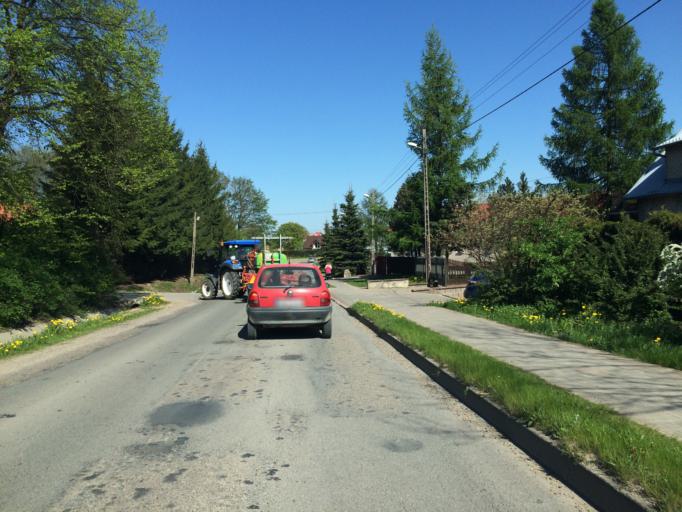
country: PL
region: Warmian-Masurian Voivodeship
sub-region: Powiat ostrodzki
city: Ostroda
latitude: 53.6833
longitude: 19.9743
